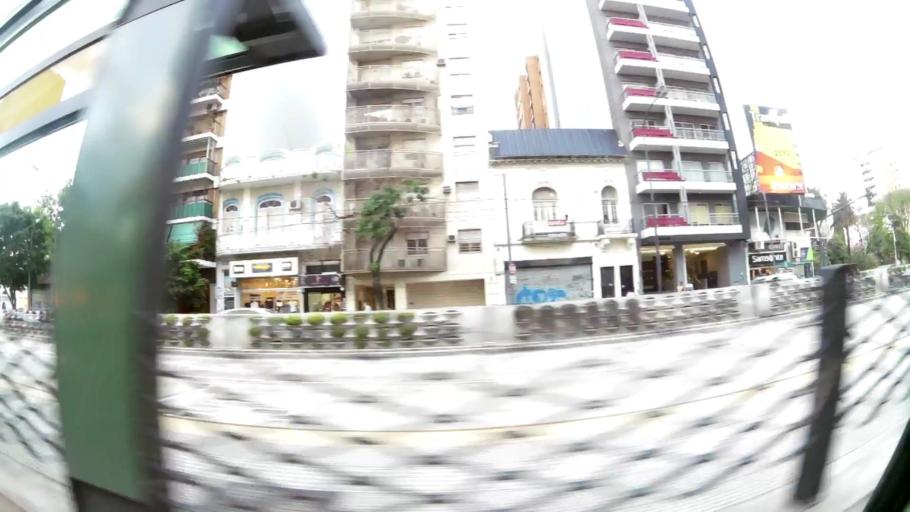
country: AR
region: Buenos Aires F.D.
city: Colegiales
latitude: -34.5473
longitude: -58.4696
